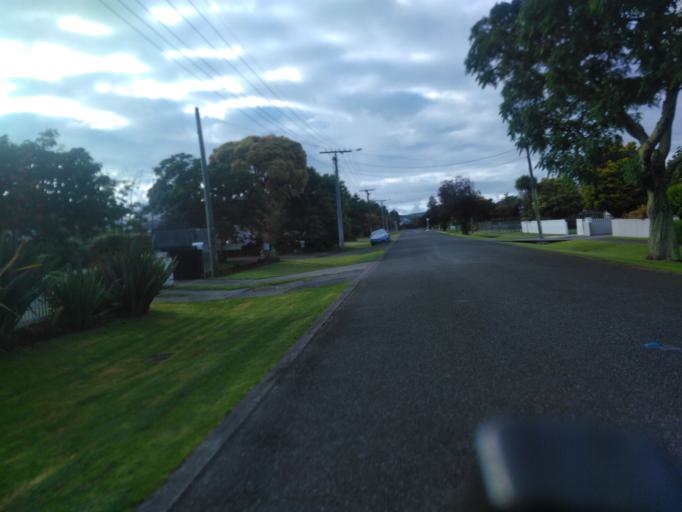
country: NZ
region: Gisborne
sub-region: Gisborne District
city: Gisborne
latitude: -38.6578
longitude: 178.0298
